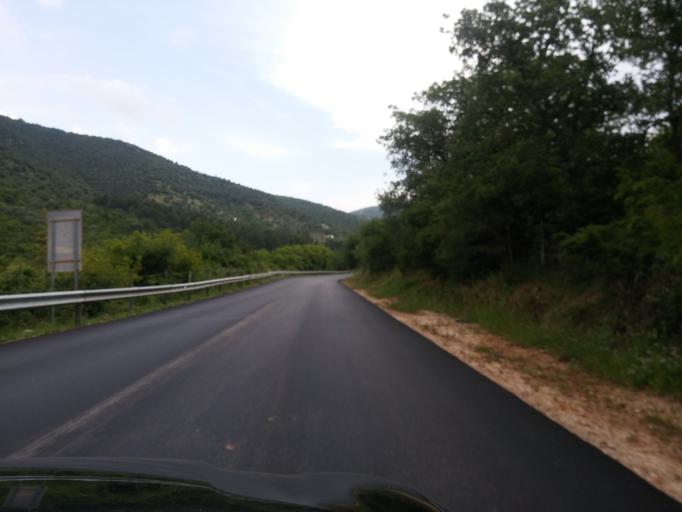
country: IT
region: Apulia
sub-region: Provincia di Foggia
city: Rignano Garganico
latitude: 41.7200
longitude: 15.5722
